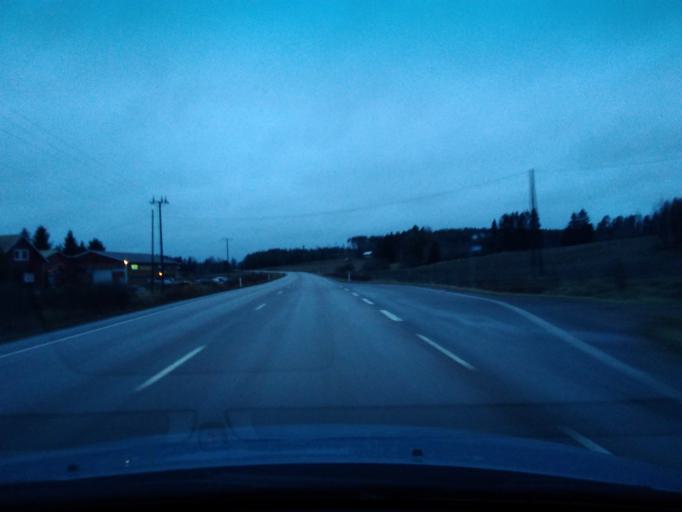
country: FI
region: Uusimaa
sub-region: Porvoo
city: Askola
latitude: 60.4610
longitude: 25.5788
